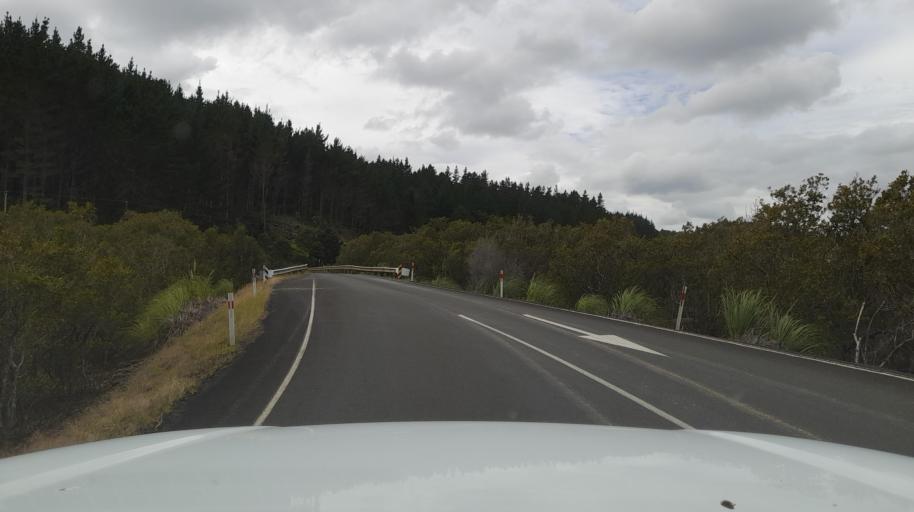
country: NZ
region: Northland
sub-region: Far North District
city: Kaitaia
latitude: -35.3637
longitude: 173.4411
